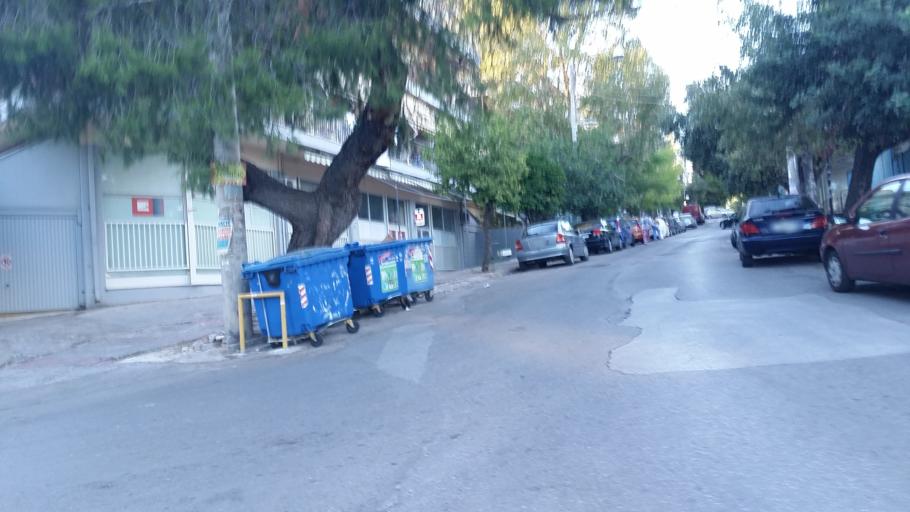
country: GR
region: Attica
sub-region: Nomarchia Athinas
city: Irakleio
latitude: 38.0485
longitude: 23.7595
